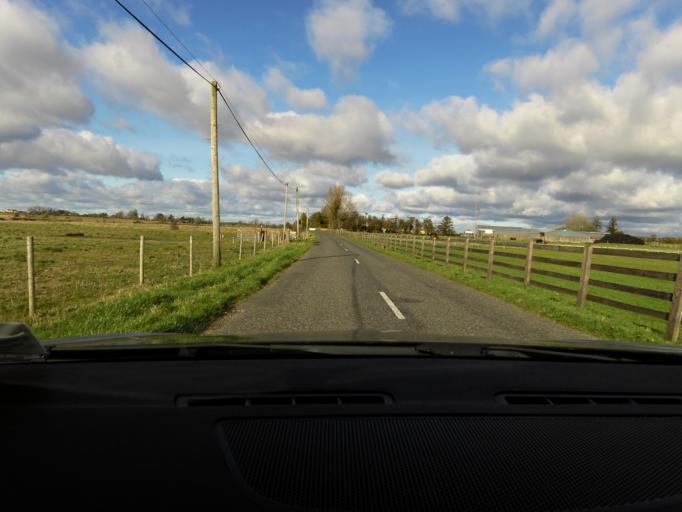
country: IE
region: Connaught
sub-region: County Galway
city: Athenry
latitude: 53.4328
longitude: -8.5703
